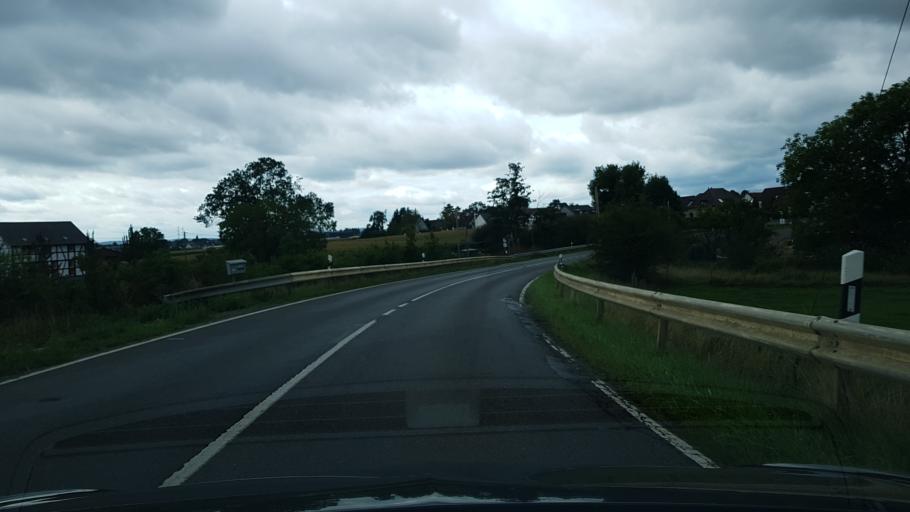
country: DE
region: North Rhine-Westphalia
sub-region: Regierungsbezirk Koln
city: Wachtberg
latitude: 50.6099
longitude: 7.0921
